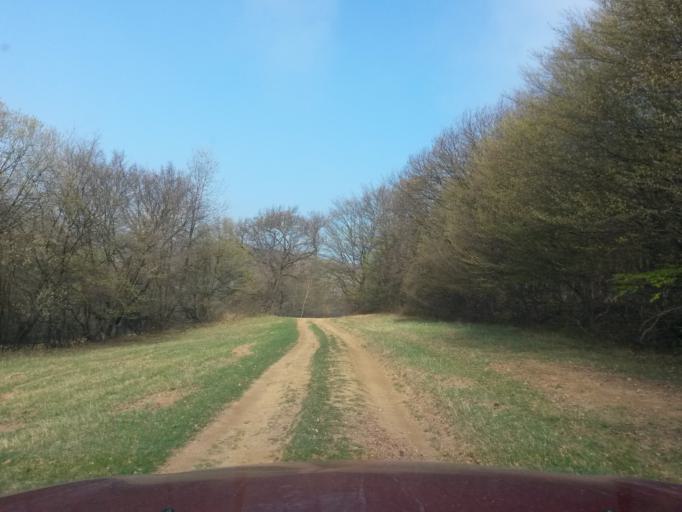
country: SK
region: Presovsky
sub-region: Okres Presov
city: Presov
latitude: 48.9228
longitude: 21.1663
